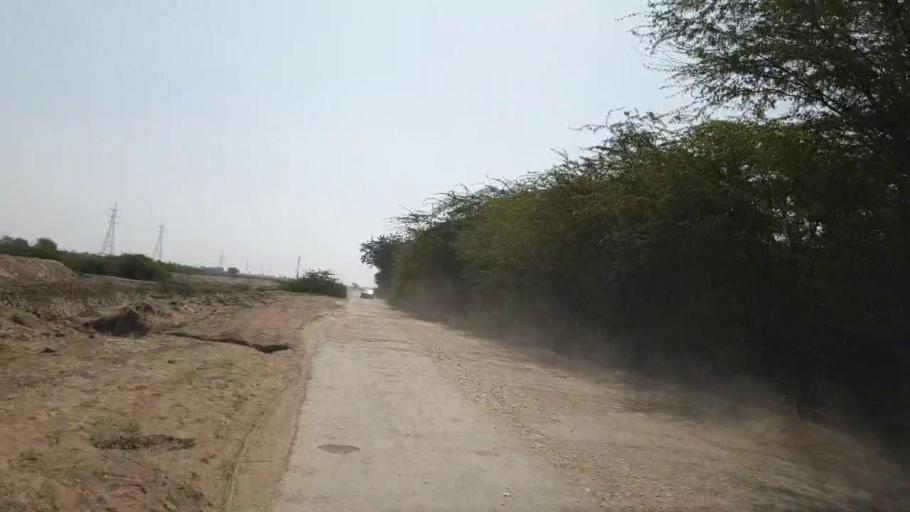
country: PK
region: Sindh
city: Naukot
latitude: 25.0087
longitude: 69.4597
